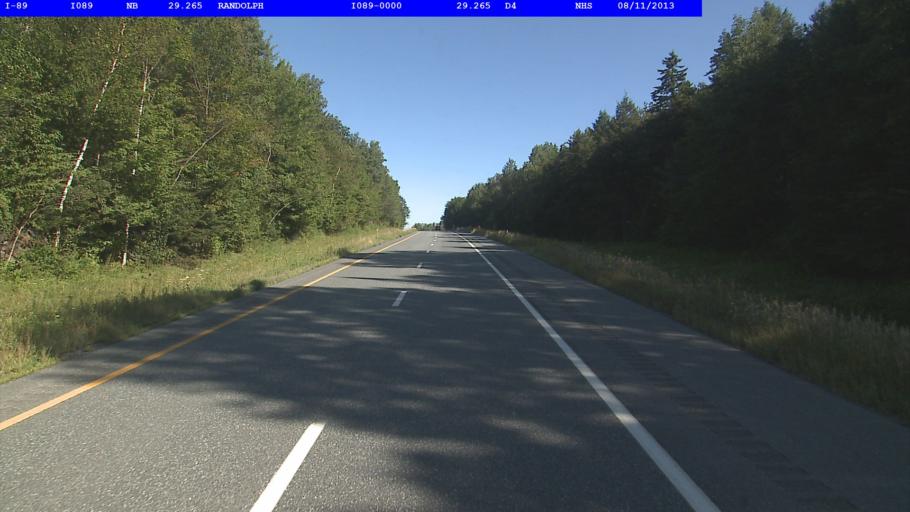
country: US
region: Vermont
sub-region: Orange County
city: Randolph
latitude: 43.9218
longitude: -72.6140
